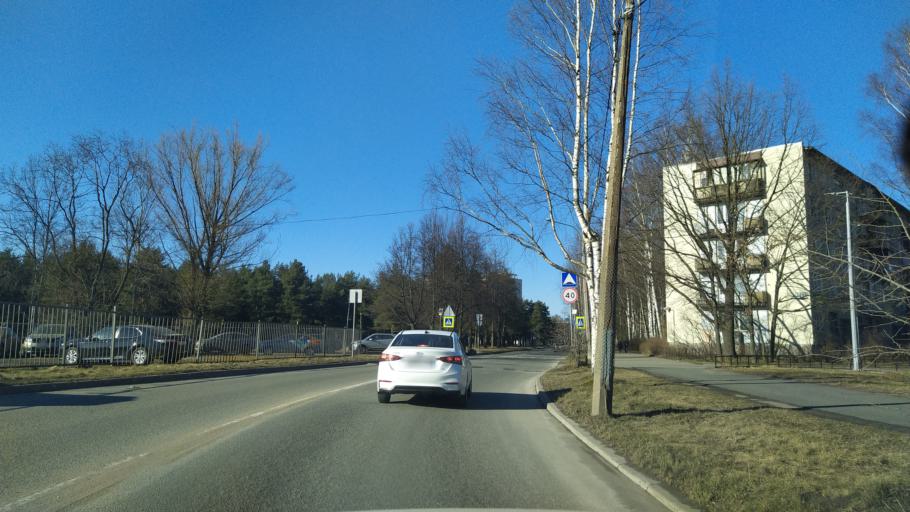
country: RU
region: Leningrad
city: Akademicheskoe
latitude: 60.0013
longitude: 30.4221
